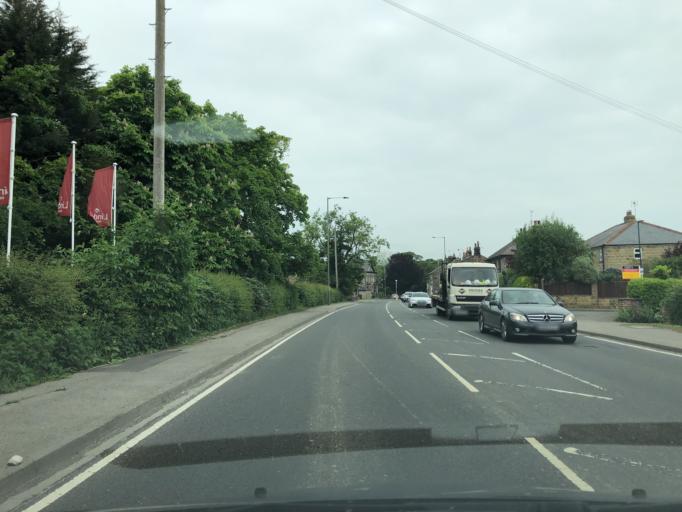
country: GB
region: England
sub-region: North Yorkshire
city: Harrogate
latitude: 54.0198
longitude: -1.5635
